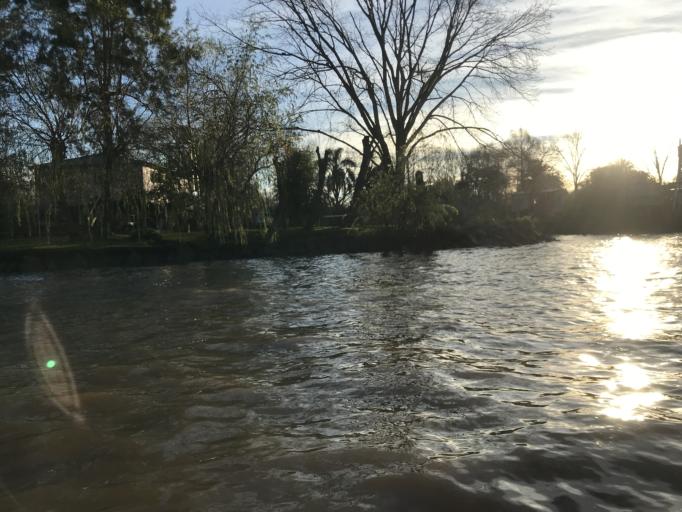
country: AR
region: Buenos Aires
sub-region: Partido de Tigre
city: Tigre
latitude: -34.3999
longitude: -58.5735
